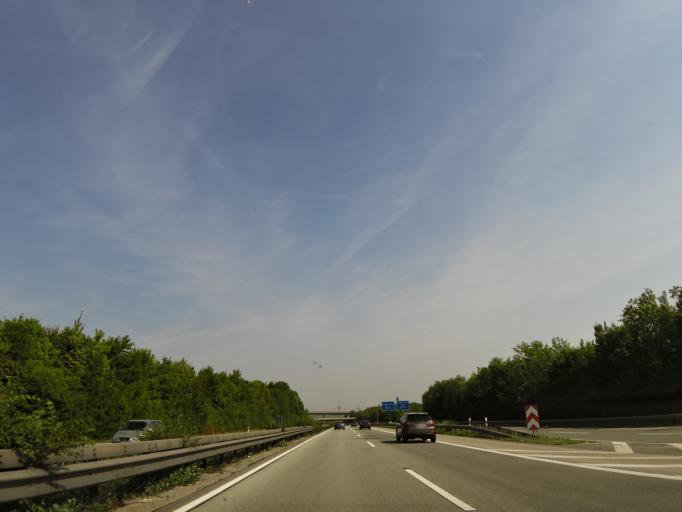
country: DE
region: Rheinland-Pfalz
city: Albig
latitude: 49.7699
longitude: 8.1118
